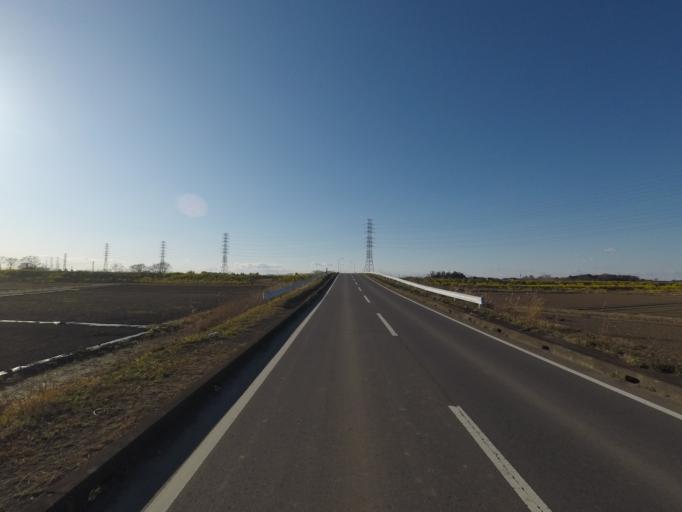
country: JP
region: Ibaraki
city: Ishige
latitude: 36.1742
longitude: 140.0130
